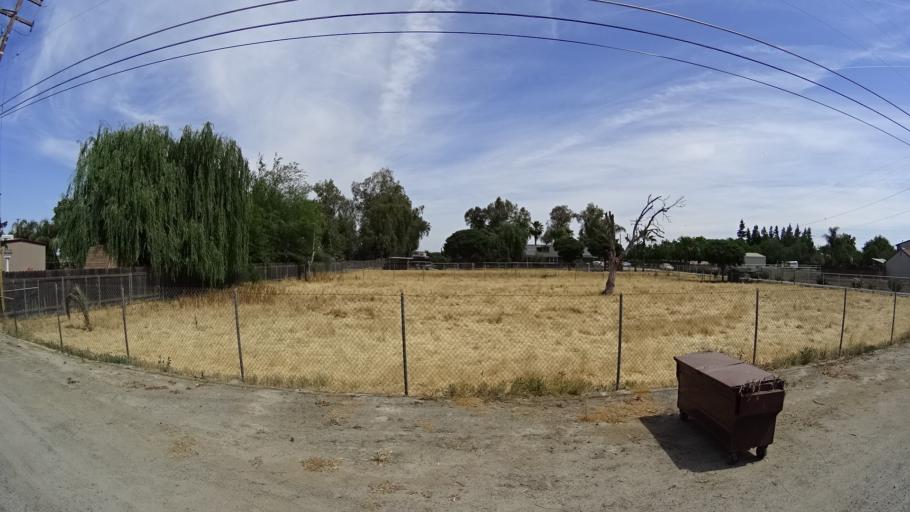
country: US
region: California
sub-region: Kings County
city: Armona
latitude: 36.3162
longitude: -119.6898
